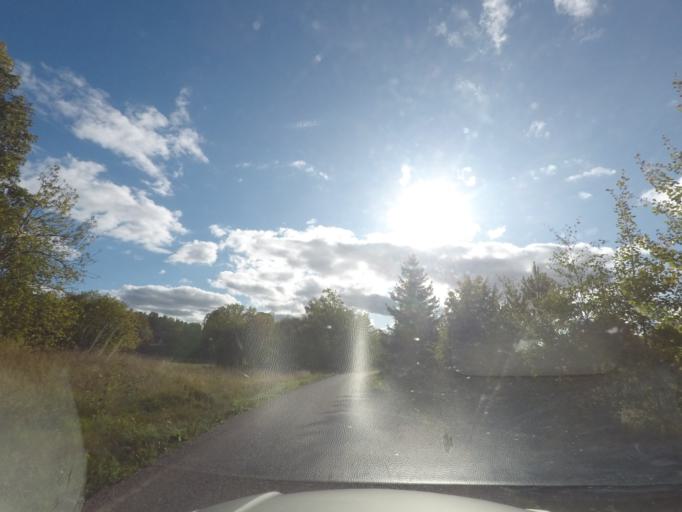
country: SE
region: Vaestmanland
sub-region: Hallstahammars Kommun
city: Kolback
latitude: 59.4992
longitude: 16.1895
